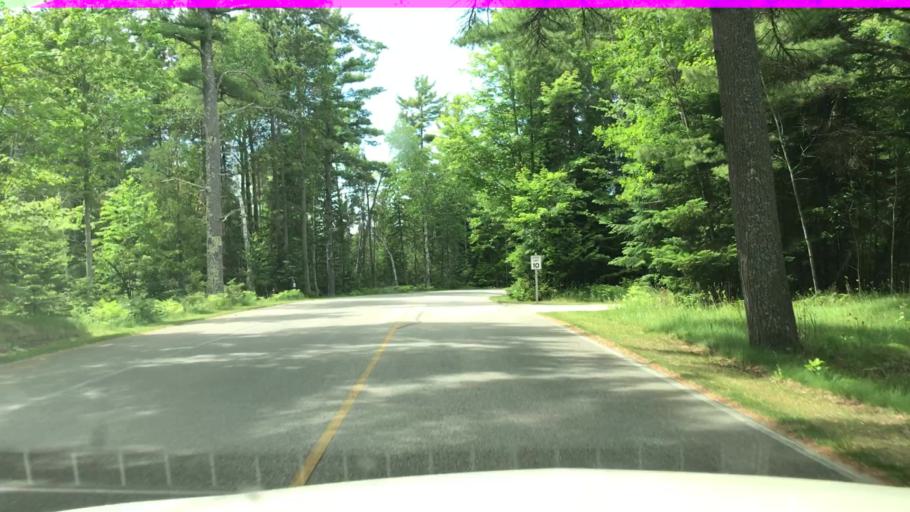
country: US
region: Michigan
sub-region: Schoolcraft County
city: Manistique
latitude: 45.9415
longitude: -86.3332
